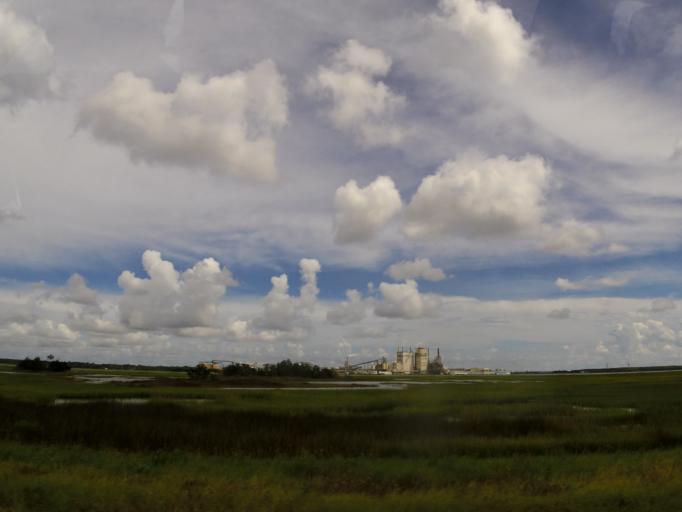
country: US
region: Georgia
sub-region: Glynn County
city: Dock Junction
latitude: 31.1816
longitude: -81.5344
